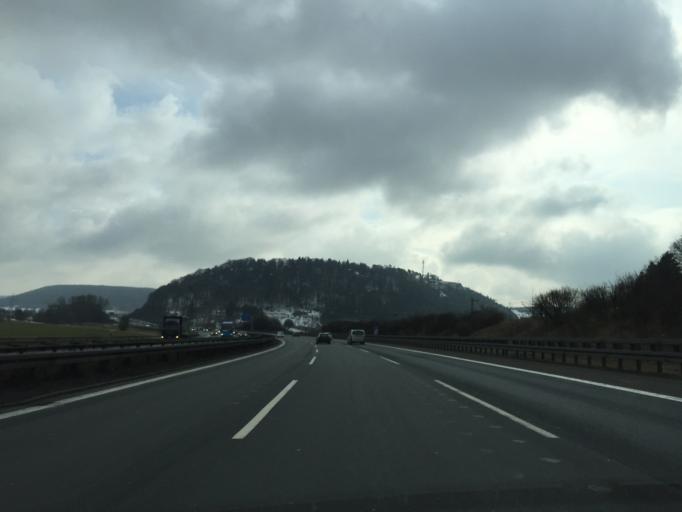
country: DE
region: Bavaria
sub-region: Regierungsbezirk Mittelfranken
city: Greding
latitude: 49.0023
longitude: 11.3582
